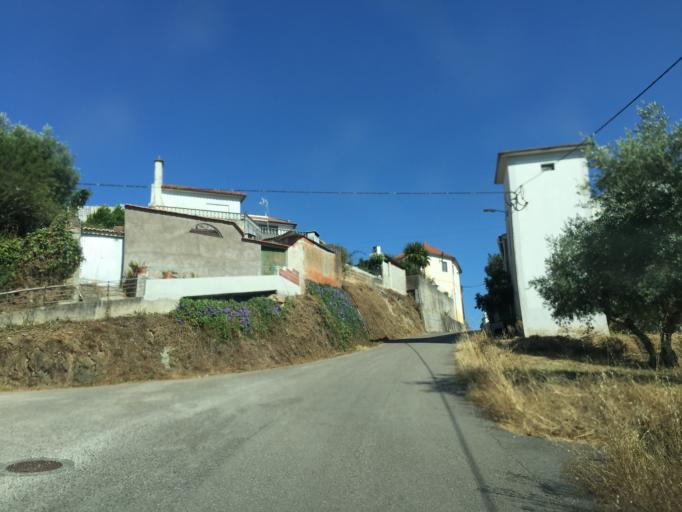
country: PT
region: Santarem
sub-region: Tomar
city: Tomar
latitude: 39.6082
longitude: -8.3327
